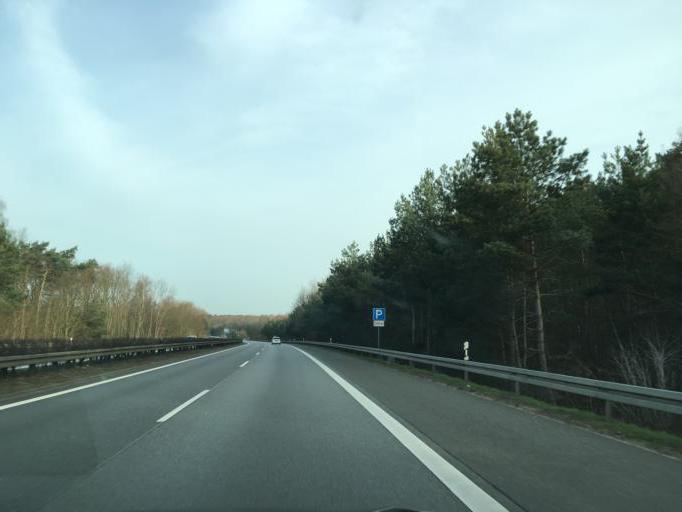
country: DE
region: Berlin
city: Blankenfelde
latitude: 52.6728
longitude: 13.4003
